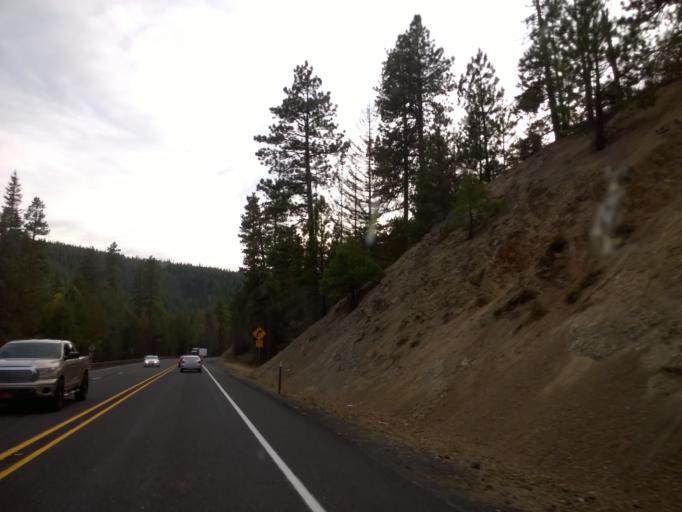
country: US
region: Washington
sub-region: Chelan County
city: Cashmere
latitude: 47.3340
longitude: -120.5972
